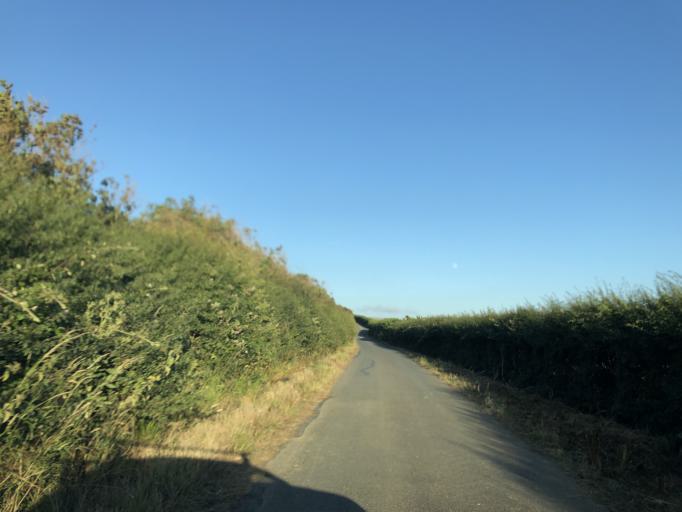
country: GB
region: England
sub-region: Isle of Wight
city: Shalfleet
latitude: 50.6352
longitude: -1.3916
